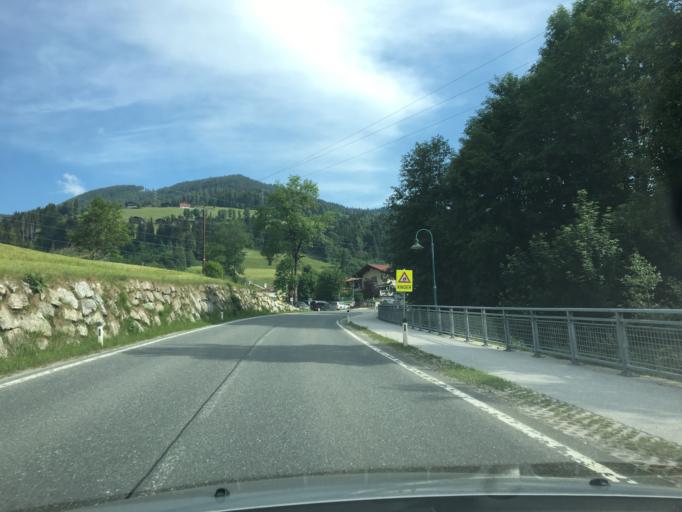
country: AT
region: Salzburg
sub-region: Politischer Bezirk Sankt Johann im Pongau
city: Wagrain
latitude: 47.3455
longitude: 13.3071
